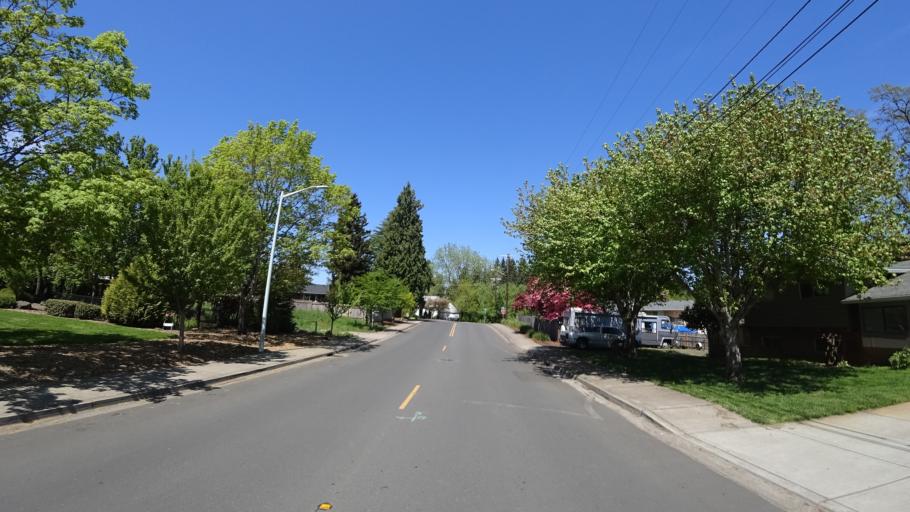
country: US
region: Oregon
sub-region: Washington County
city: Hillsboro
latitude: 45.5179
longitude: -122.9640
